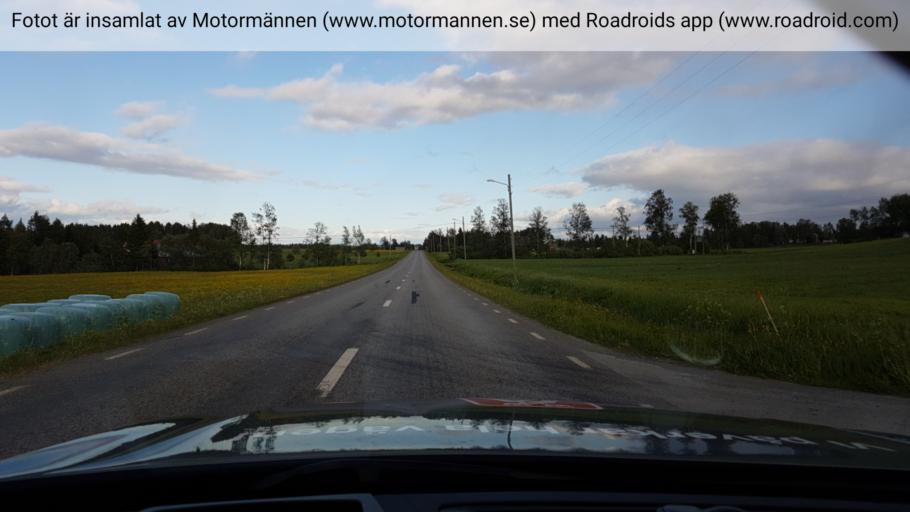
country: SE
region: Jaemtland
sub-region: Krokoms Kommun
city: Krokom
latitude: 63.1486
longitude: 14.1676
